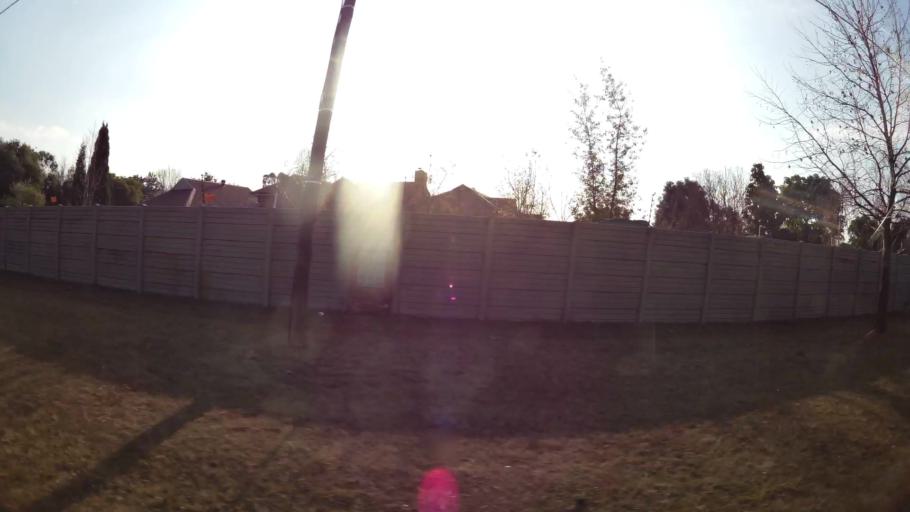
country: ZA
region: Gauteng
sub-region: Ekurhuleni Metropolitan Municipality
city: Benoni
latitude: -26.1403
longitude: 28.3644
